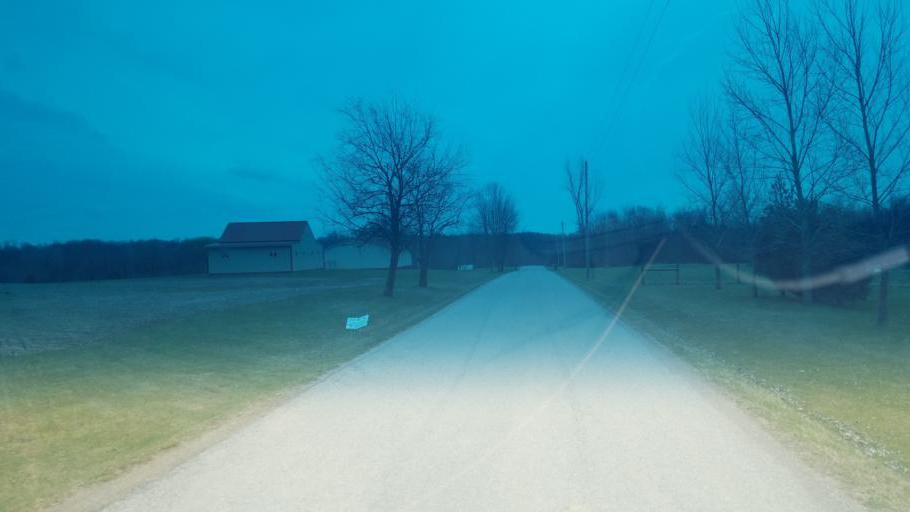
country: US
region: Ohio
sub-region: Knox County
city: Centerburg
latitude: 40.3641
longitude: -82.6566
